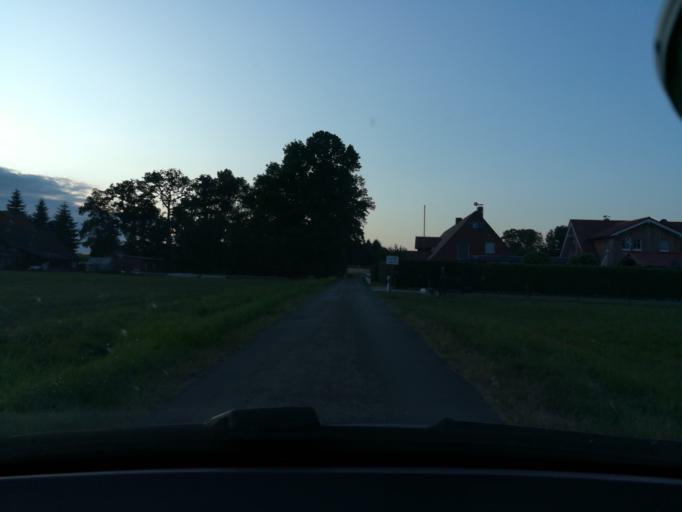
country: DE
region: North Rhine-Westphalia
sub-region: Regierungsbezirk Munster
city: Lienen
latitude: 52.1356
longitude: 7.9800
